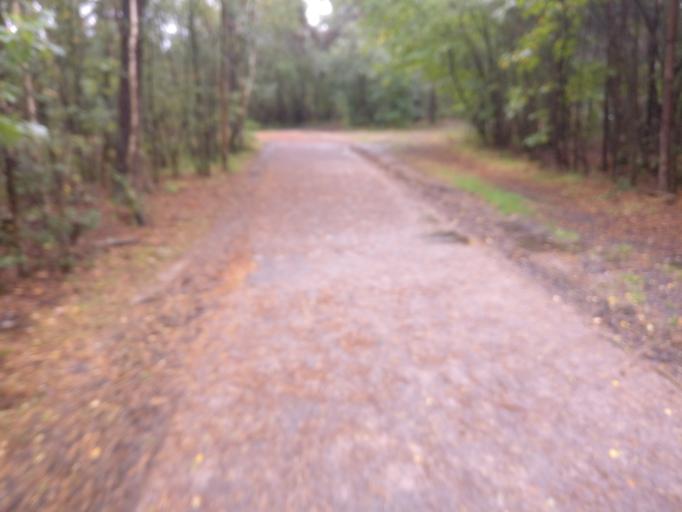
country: GB
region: England
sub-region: Surrey
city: Frimley
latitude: 51.3172
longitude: -0.7102
